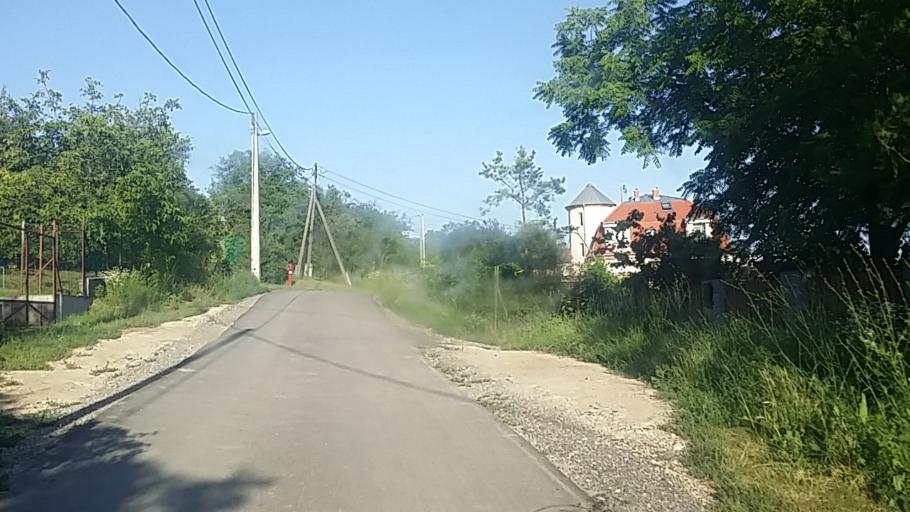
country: HU
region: Pest
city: Urom
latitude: 47.5782
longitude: 19.0195
